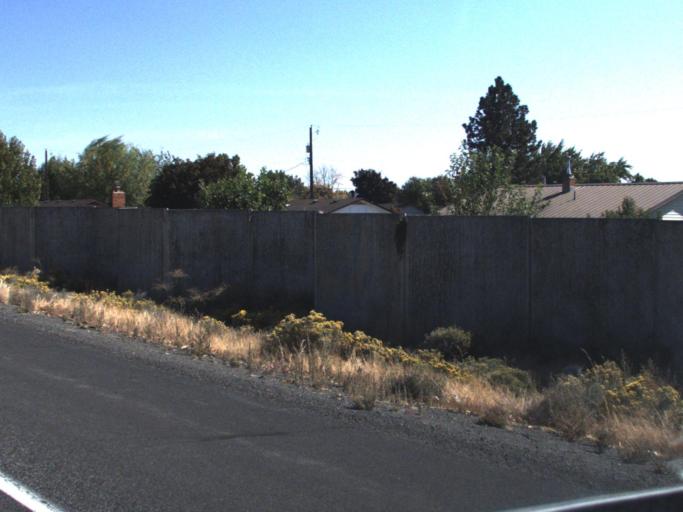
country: US
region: Washington
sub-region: Franklin County
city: Pasco
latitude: 46.2484
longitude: -119.1027
